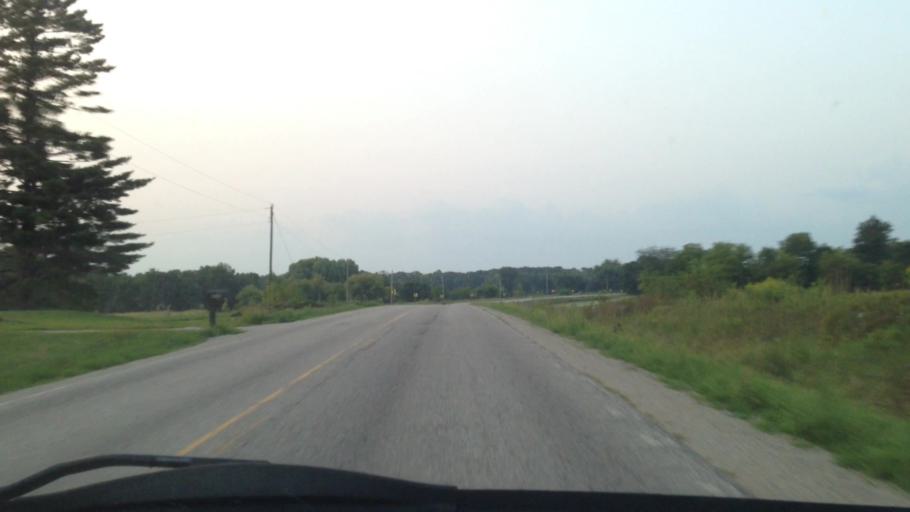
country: US
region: Iowa
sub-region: Benton County
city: Urbana
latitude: 42.1477
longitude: -91.8792
